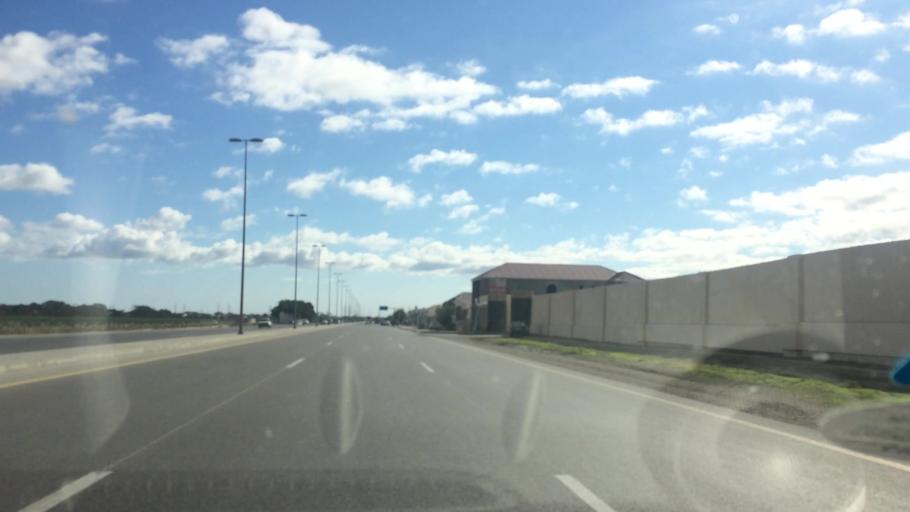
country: AZ
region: Baki
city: Qala
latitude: 40.4470
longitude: 50.1667
